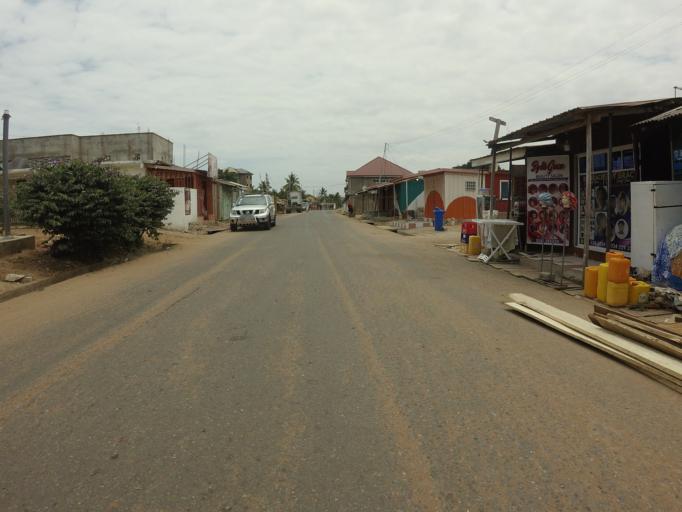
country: GH
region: Greater Accra
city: Nungua
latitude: 5.6043
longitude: -0.0883
